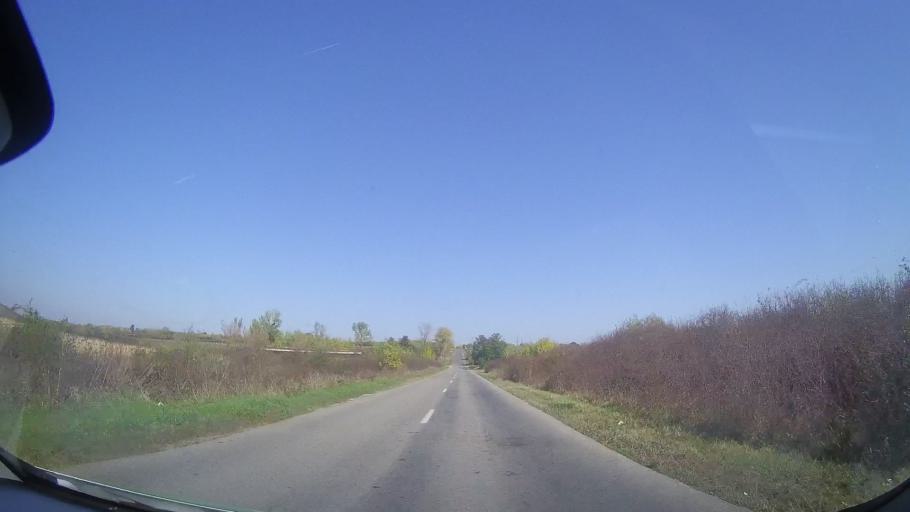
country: RO
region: Timis
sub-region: Comuna Costeiu
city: Costeiu
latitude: 45.7540
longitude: 21.8473
